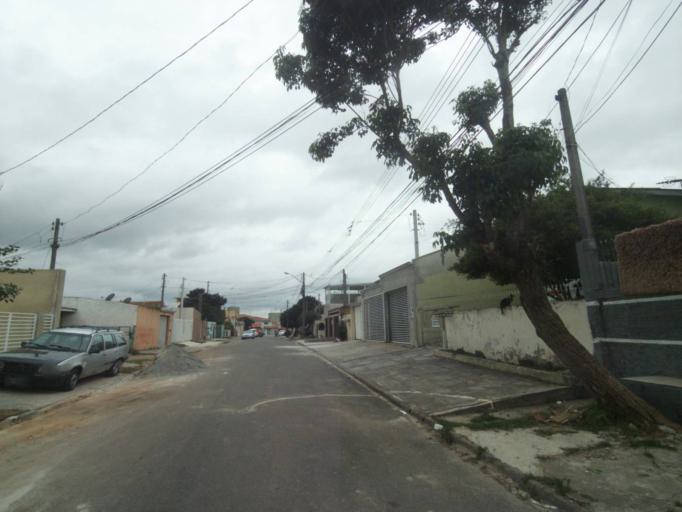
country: BR
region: Parana
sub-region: Sao Jose Dos Pinhais
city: Sao Jose dos Pinhais
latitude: -25.5449
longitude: -49.2693
